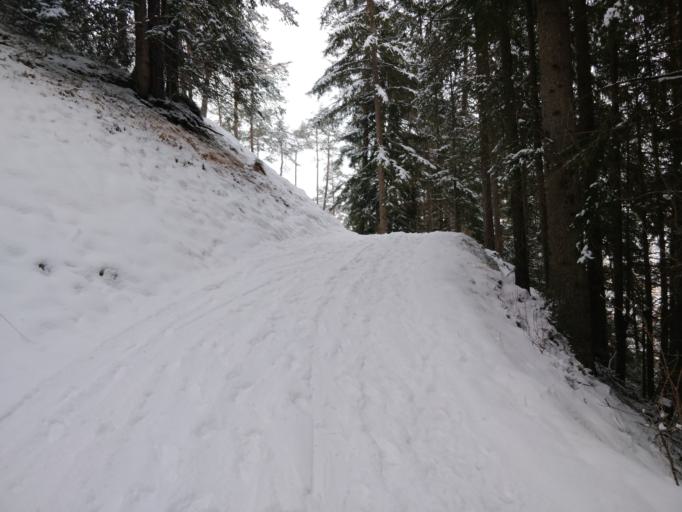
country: IT
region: Trentino-Alto Adige
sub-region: Bolzano
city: San Vigilio
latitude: 46.6949
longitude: 11.9297
